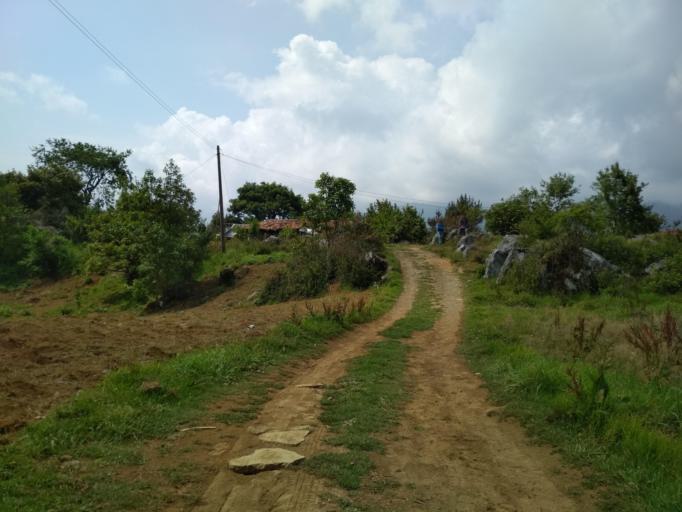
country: MX
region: Veracruz
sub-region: Camerino Z. Mendoza
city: Necoxtla
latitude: 18.7653
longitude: -97.1455
